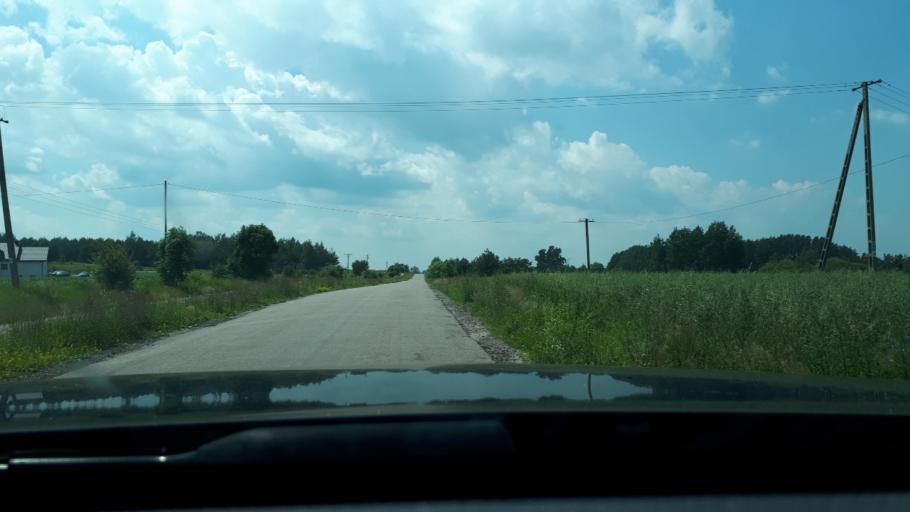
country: PL
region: Podlasie
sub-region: Powiat bialostocki
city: Choroszcz
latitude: 53.1197
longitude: 22.8945
